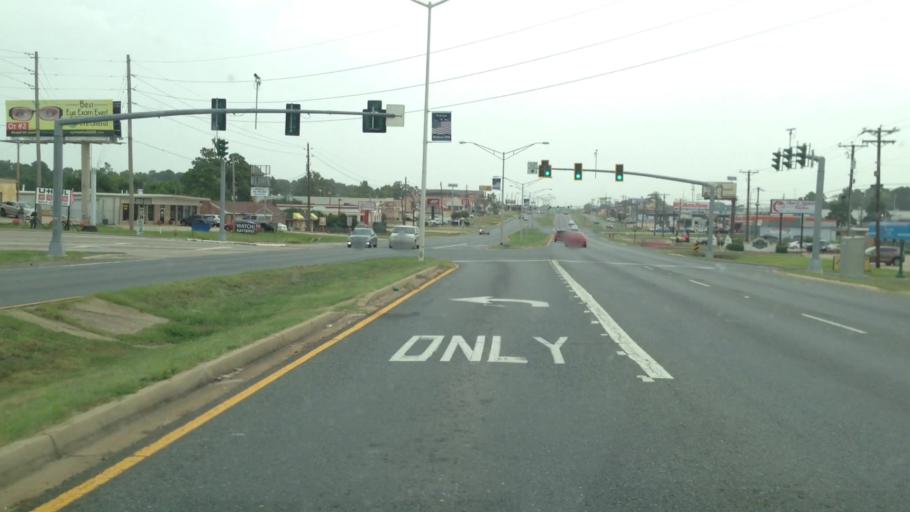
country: US
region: Louisiana
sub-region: De Soto Parish
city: Stonewall
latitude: 32.3955
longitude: -93.8107
